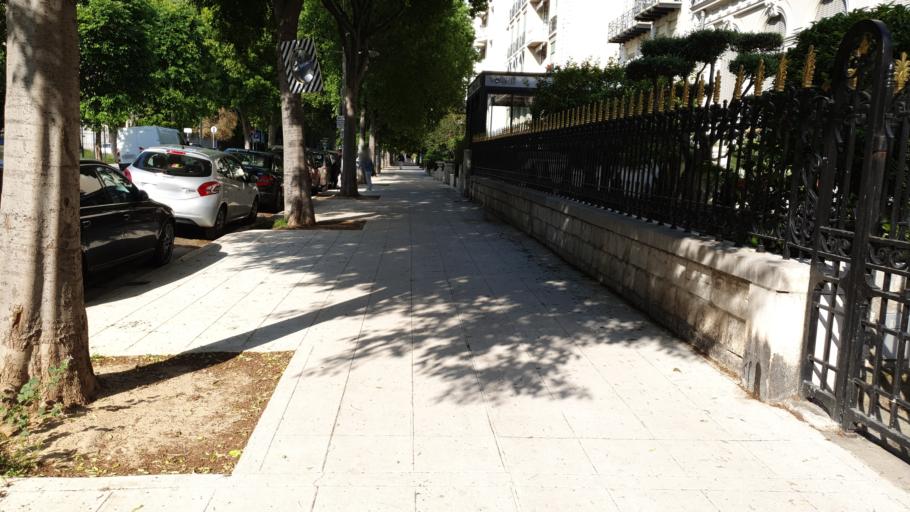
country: FR
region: Provence-Alpes-Cote d'Azur
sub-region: Departement des Alpes-Maritimes
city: Nice
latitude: 43.6994
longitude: 7.2640
